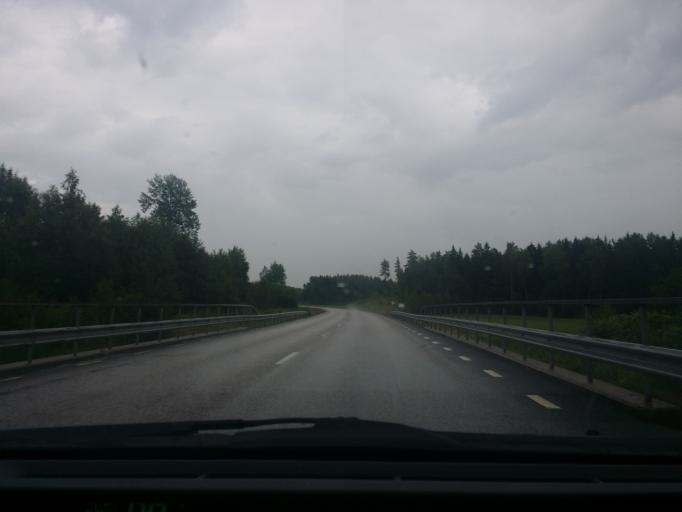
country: SE
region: OErebro
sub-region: Lindesbergs Kommun
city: Frovi
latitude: 59.4592
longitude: 15.4422
